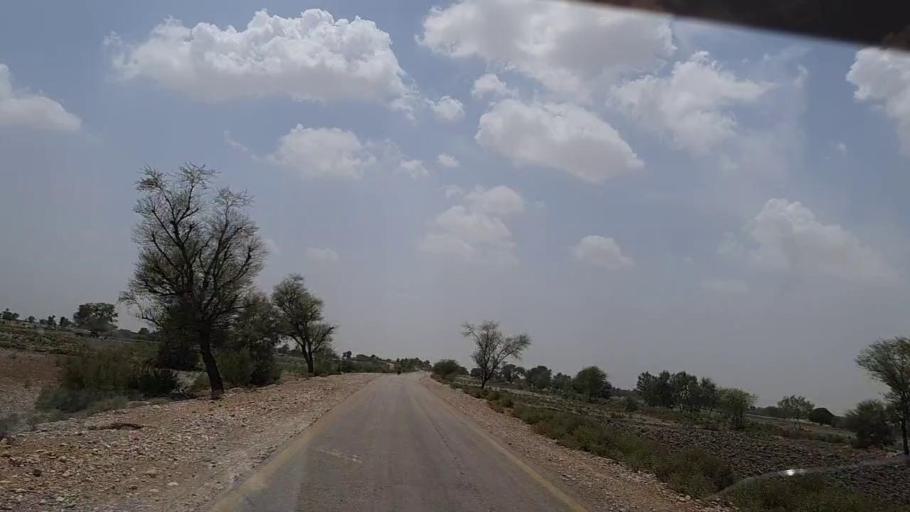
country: PK
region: Sindh
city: Bhan
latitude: 26.5415
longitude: 67.6426
